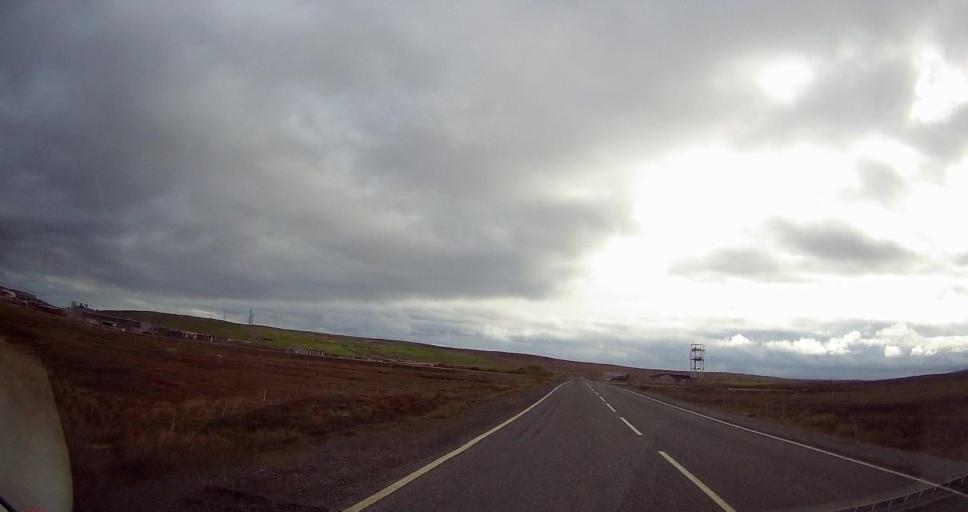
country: GB
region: Scotland
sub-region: Shetland Islands
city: Lerwick
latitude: 60.4383
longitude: -1.2765
